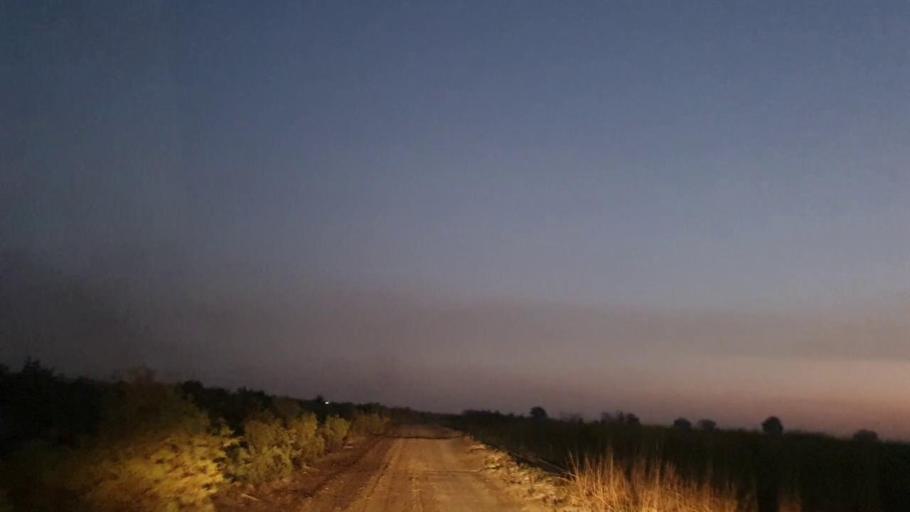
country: PK
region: Sindh
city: Nawabshah
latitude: 26.3275
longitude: 68.3765
